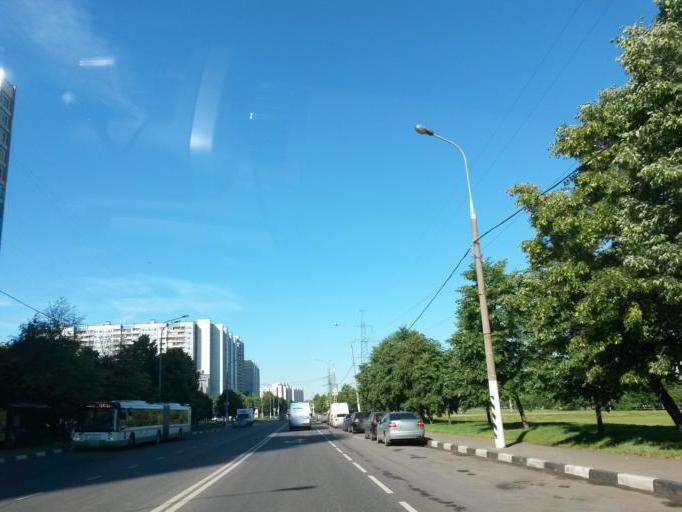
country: RU
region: Moscow
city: Brateyevo
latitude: 55.6414
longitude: 37.7603
